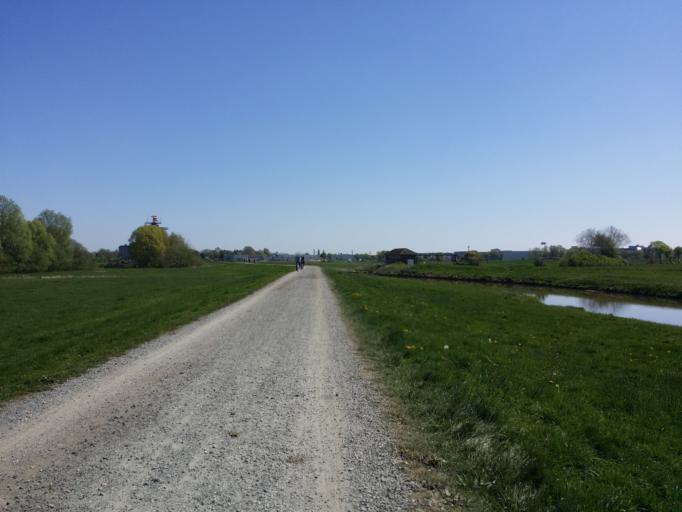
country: DE
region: Bremen
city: Bremen
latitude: 53.0365
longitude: 8.7922
